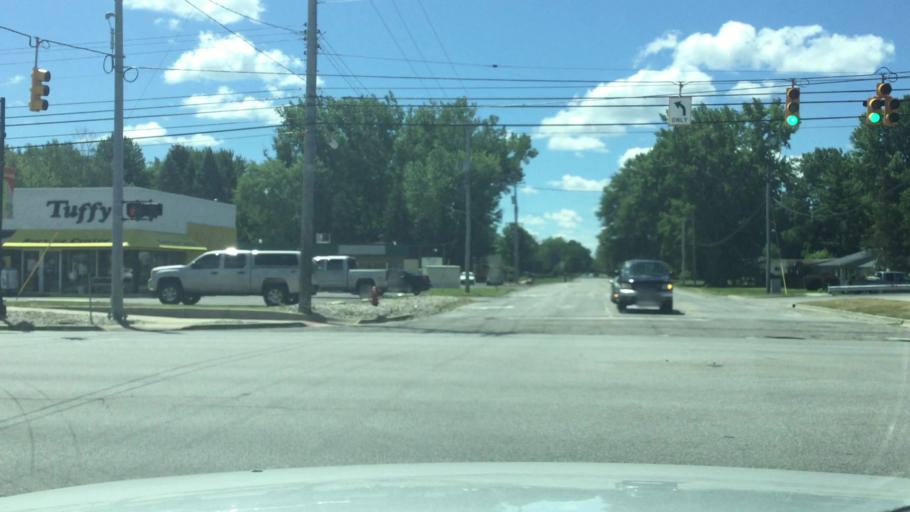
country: US
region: Michigan
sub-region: Saginaw County
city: Shields
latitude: 43.4161
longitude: -84.0715
